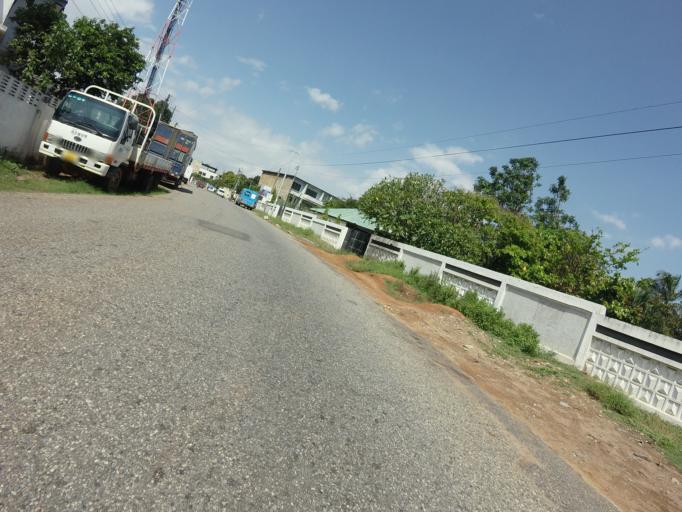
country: GH
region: Greater Accra
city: Accra
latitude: 5.5761
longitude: -0.1994
